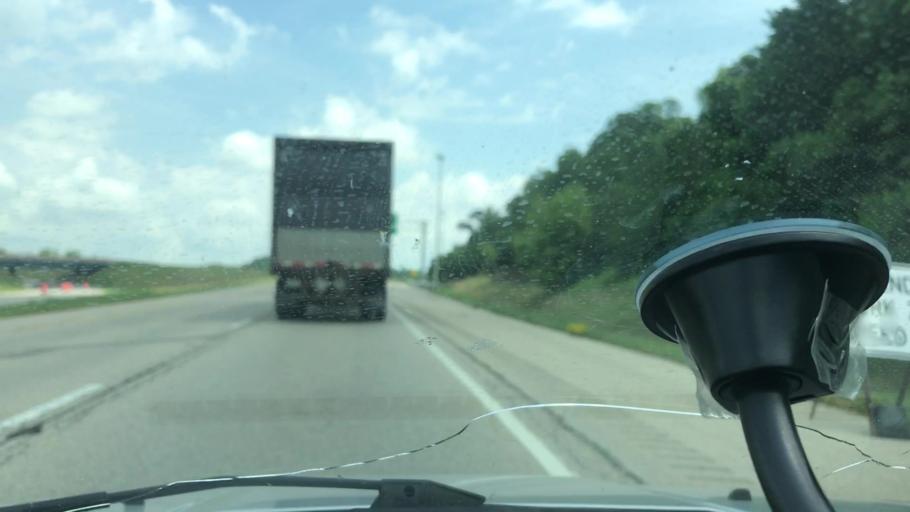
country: US
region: Illinois
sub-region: Peoria County
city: Bellevue
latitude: 40.7358
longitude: -89.6704
